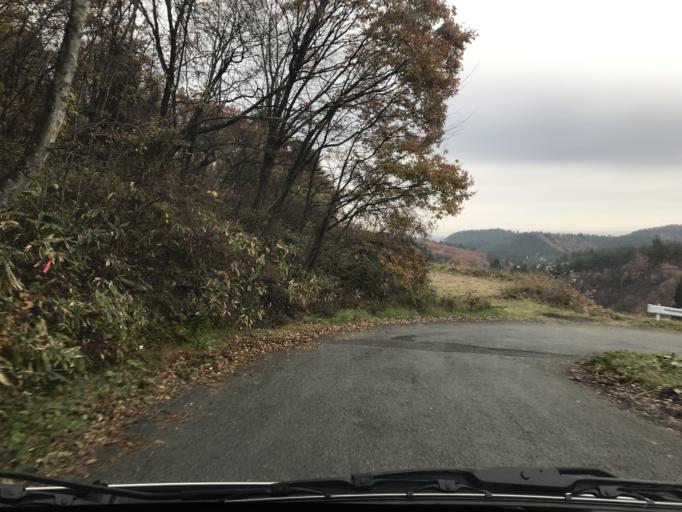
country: JP
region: Iwate
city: Ichinoseki
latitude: 39.0005
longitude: 141.0260
